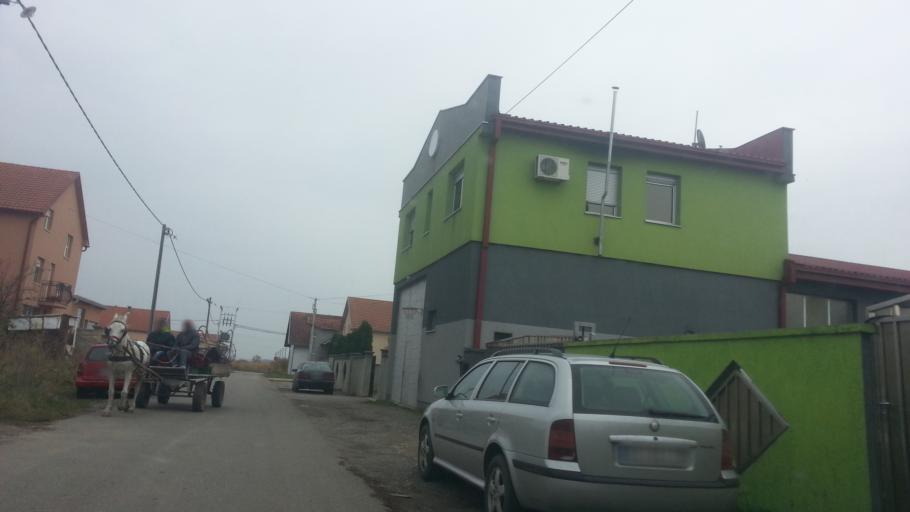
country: RS
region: Autonomna Pokrajina Vojvodina
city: Nova Pazova
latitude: 44.9565
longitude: 20.2090
